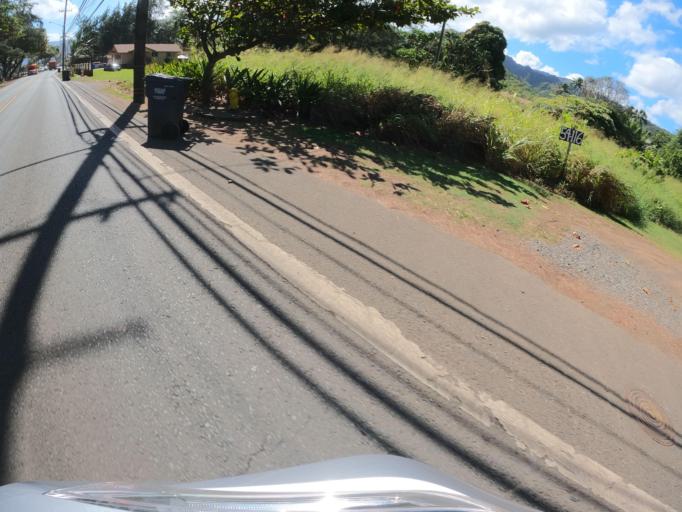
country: US
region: Hawaii
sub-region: Honolulu County
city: Hau'ula
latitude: 21.6103
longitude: -157.9102
